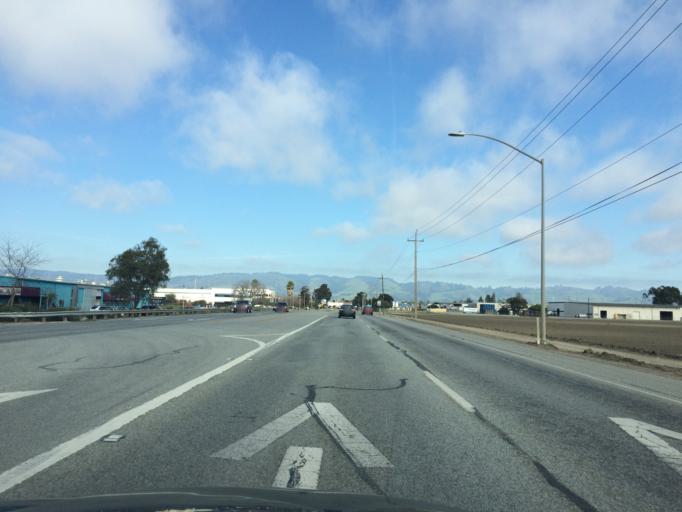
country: US
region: California
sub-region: Santa Cruz County
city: Watsonville
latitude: 36.9013
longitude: -121.7634
